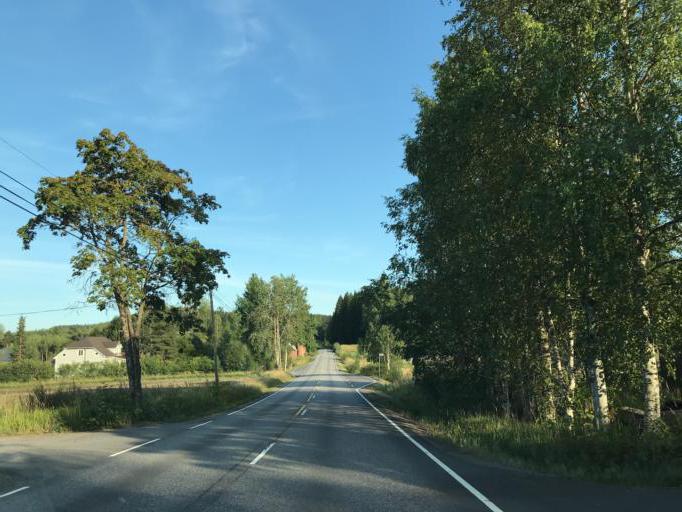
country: FI
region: Uusimaa
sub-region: Helsinki
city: Vihti
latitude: 60.4153
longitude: 24.4264
